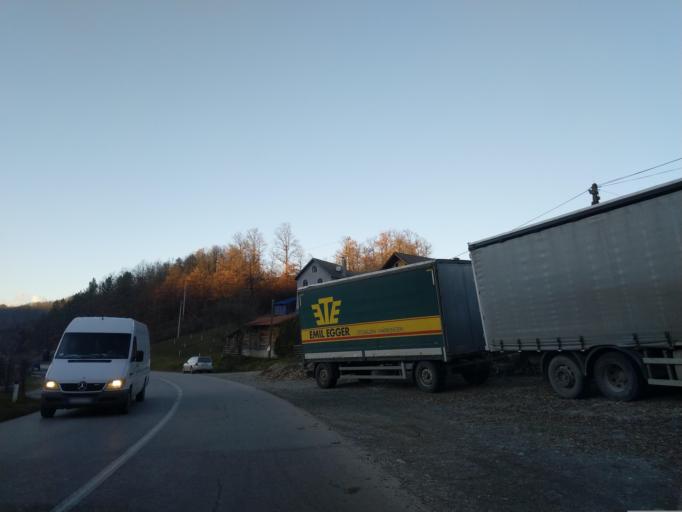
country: RS
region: Central Serbia
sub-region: Zlatiborski Okrug
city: Kosjeric
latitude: 43.9733
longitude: 19.9554
